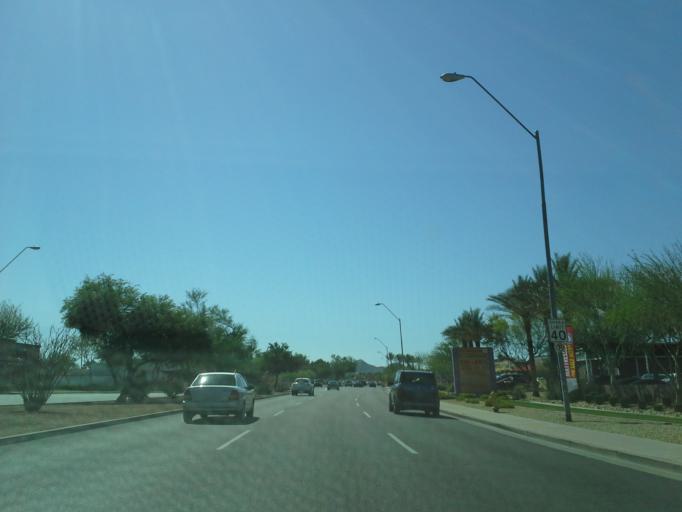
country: US
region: Arizona
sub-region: Maricopa County
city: Paradise Valley
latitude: 33.5976
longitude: -111.9765
